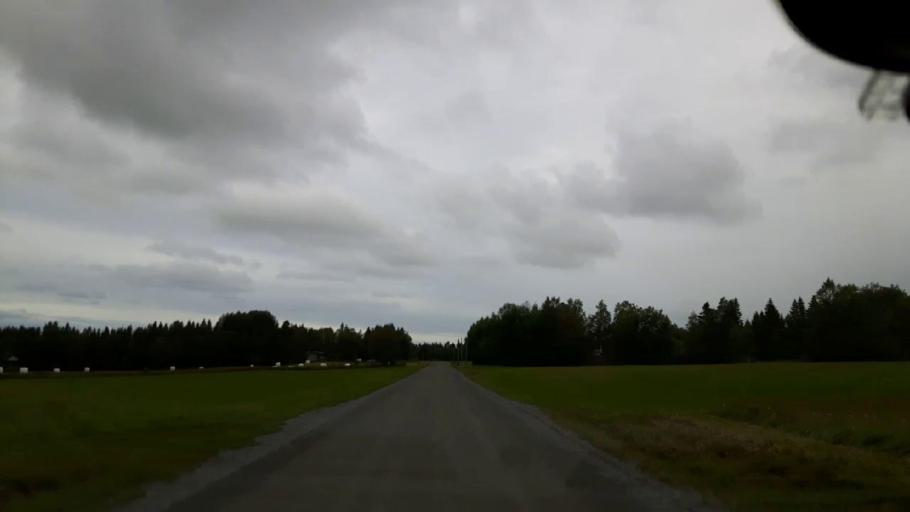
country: SE
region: Jaemtland
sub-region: OEstersunds Kommun
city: Ostersund
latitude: 63.0905
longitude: 14.5552
